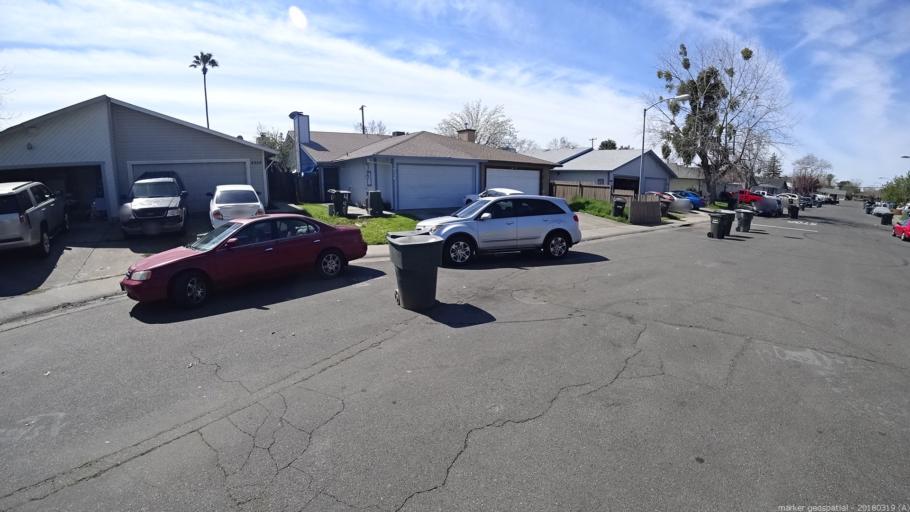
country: US
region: California
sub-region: Sacramento County
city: Parkway
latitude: 38.5125
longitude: -121.4466
